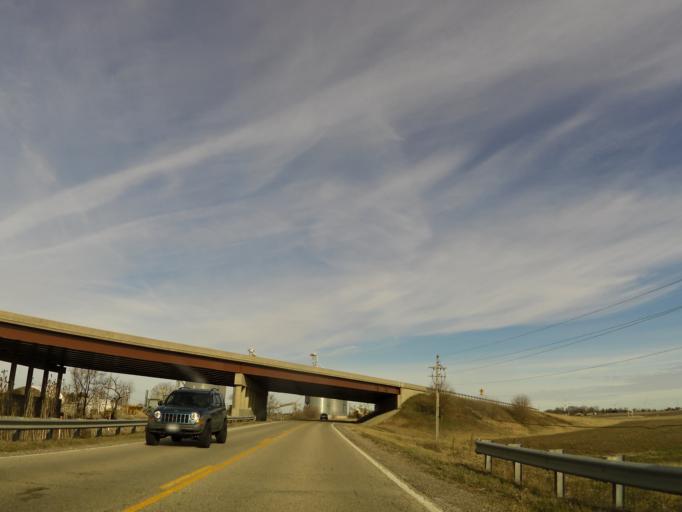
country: US
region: Illinois
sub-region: McLean County
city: Twin Grove
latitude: 40.5285
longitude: -89.0577
